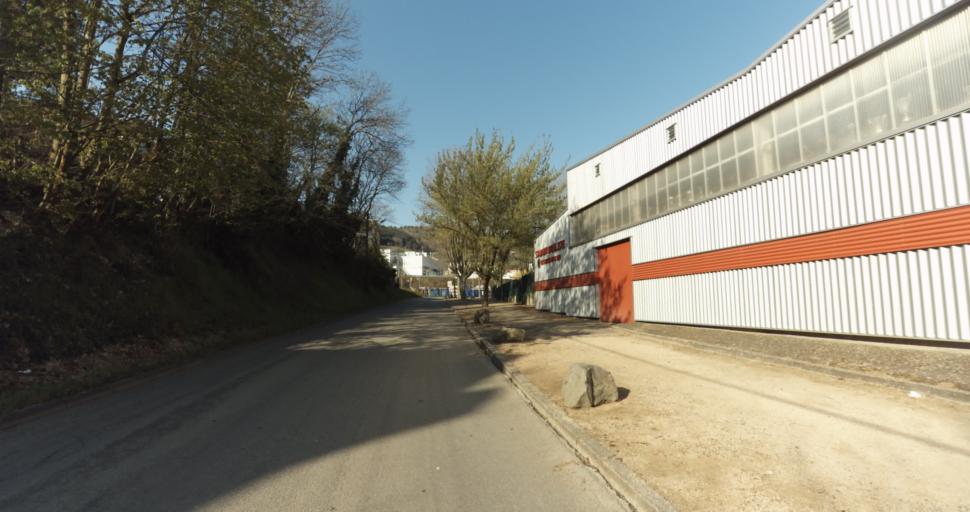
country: FR
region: Rhone-Alpes
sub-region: Departement du Rhone
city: Tarare
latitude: 45.8856
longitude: 4.4407
